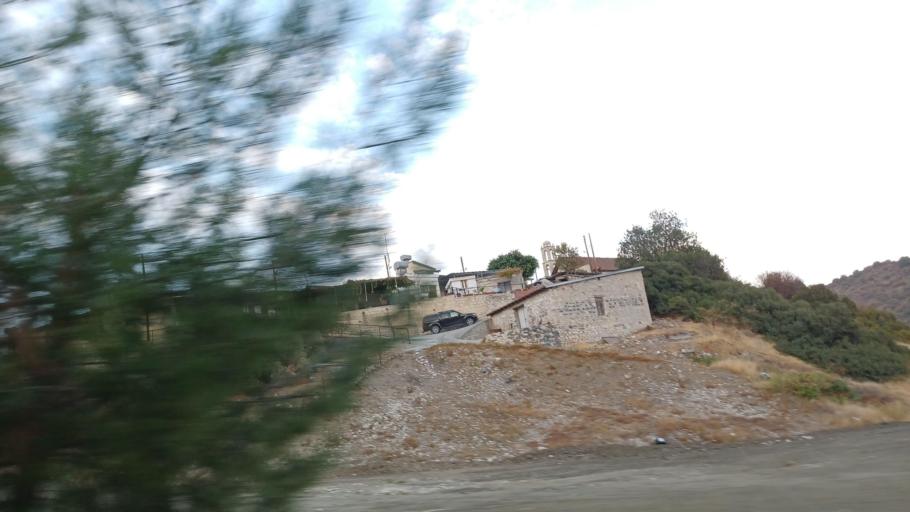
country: CY
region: Limassol
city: Pelendri
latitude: 34.8315
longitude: 32.9584
